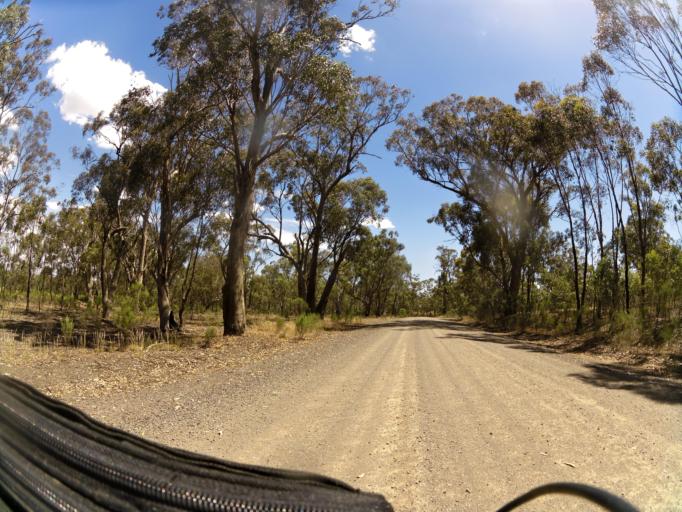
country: AU
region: Victoria
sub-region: Campaspe
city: Kyabram
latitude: -36.8044
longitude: 145.0740
